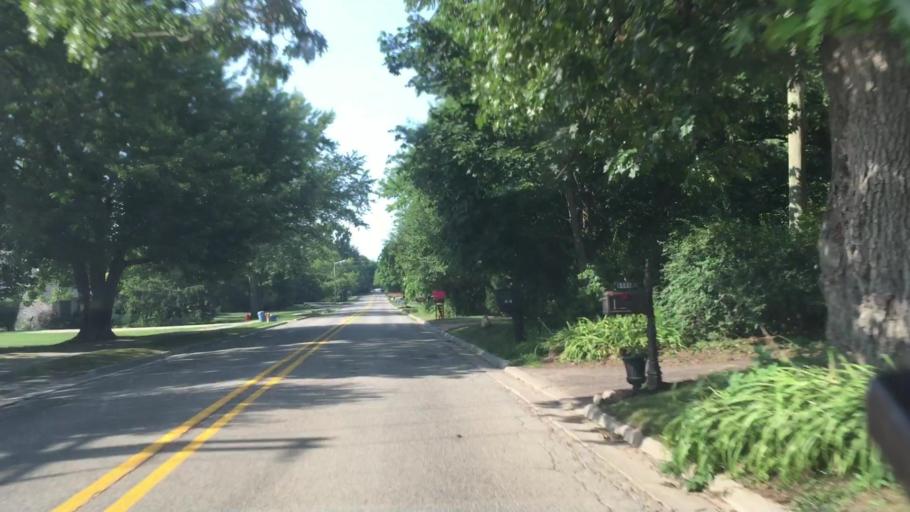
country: US
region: Michigan
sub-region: Oakland County
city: Franklin
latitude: 42.5393
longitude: -83.2967
